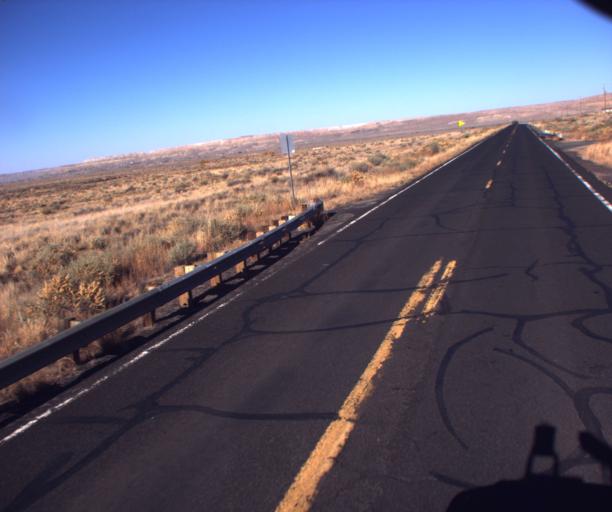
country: US
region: Arizona
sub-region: Navajo County
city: First Mesa
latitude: 35.8353
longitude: -110.2991
